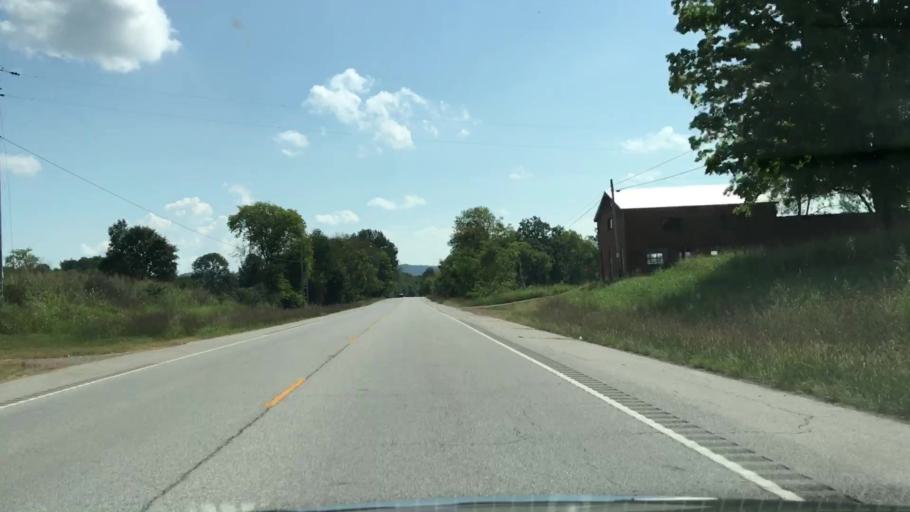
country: US
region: Tennessee
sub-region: Trousdale County
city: Hartsville
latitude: 36.3626
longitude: -86.0631
